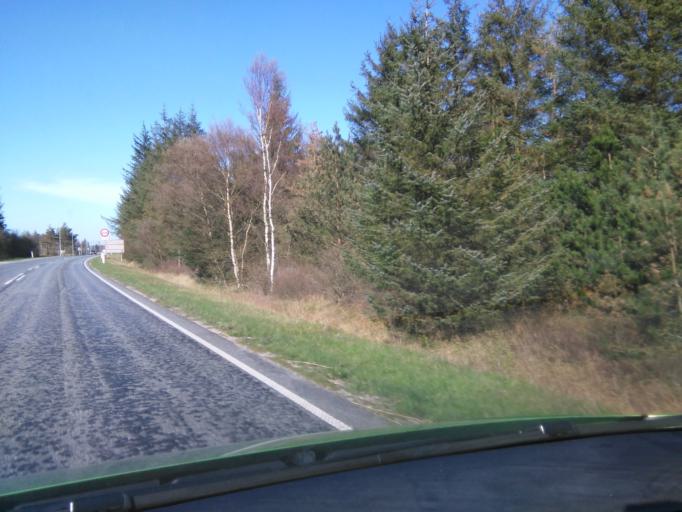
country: DK
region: South Denmark
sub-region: Varde Kommune
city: Oksbol
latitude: 55.6032
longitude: 8.2250
